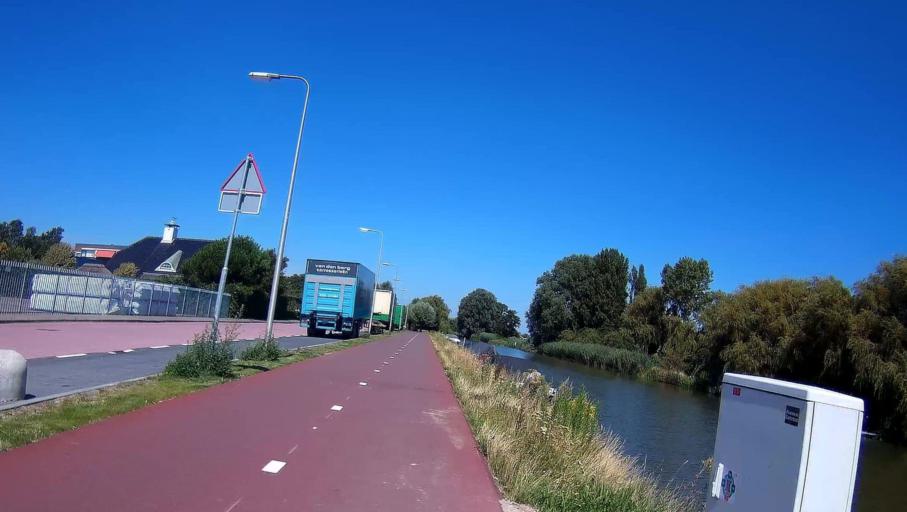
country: NL
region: South Holland
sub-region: Gemeente Westland
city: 's-Gravenzande
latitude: 51.9953
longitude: 4.1824
